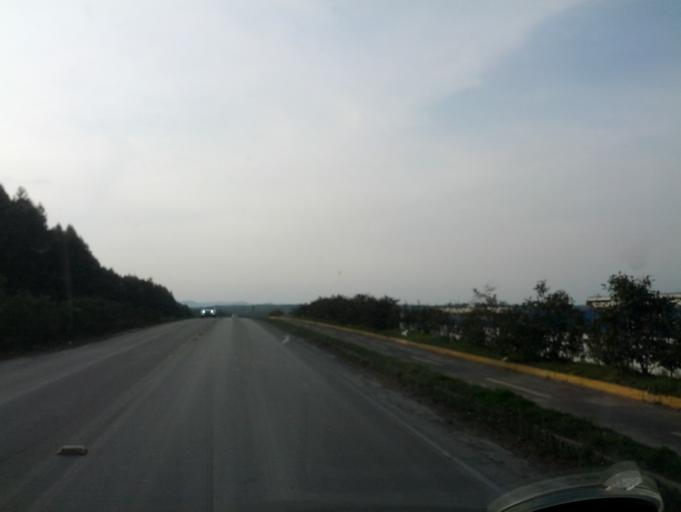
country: BR
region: Santa Catarina
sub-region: Otacilio Costa
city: Otacilio Costa
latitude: -27.4755
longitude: -50.1201
